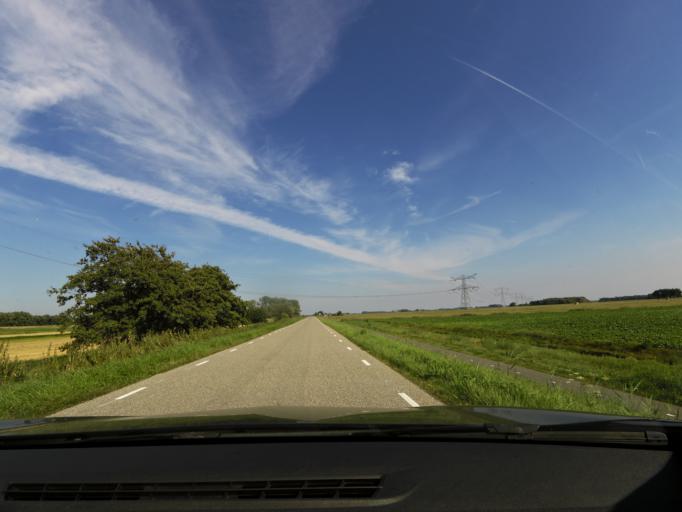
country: NL
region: South Holland
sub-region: Gemeente Sliedrecht
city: Sliedrecht
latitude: 51.7939
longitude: 4.8001
